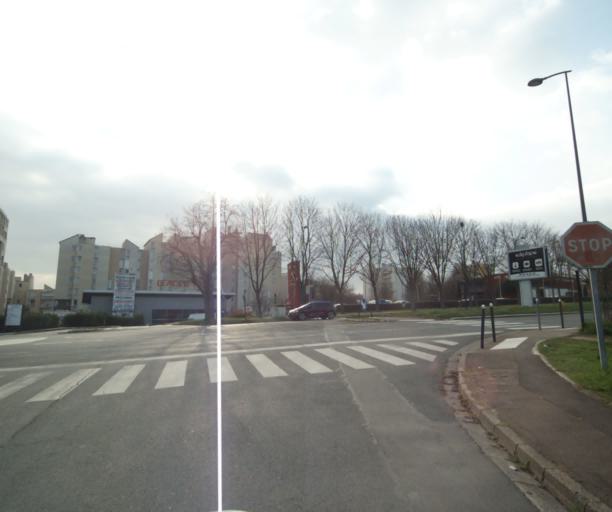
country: FR
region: Ile-de-France
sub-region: Departement du Val-d'Oise
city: Cergy-Pontoise
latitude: 49.0446
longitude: 2.0706
